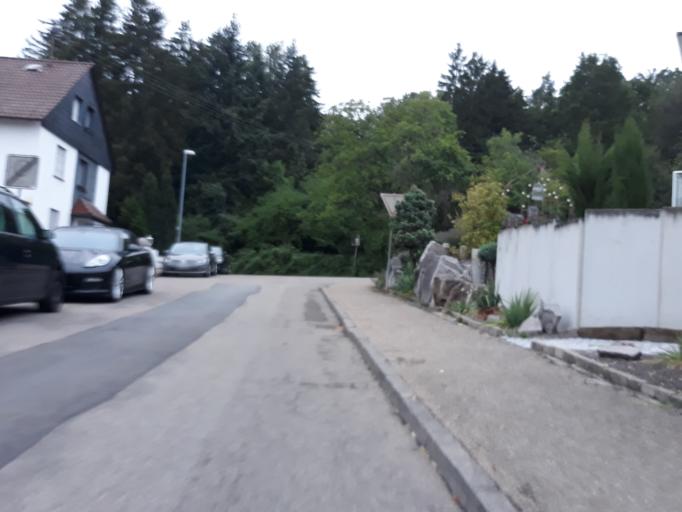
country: DE
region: Baden-Wuerttemberg
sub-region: Regierungsbezirk Stuttgart
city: Schonaich
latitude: 48.6659
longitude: 9.0515
